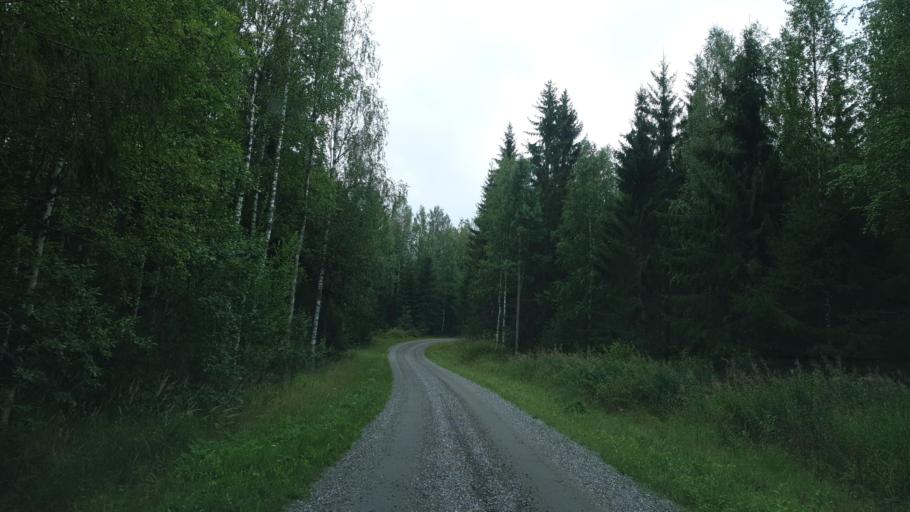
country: FI
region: Northern Savo
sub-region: Kuopio
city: Nilsiae
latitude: 63.2482
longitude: 28.2567
